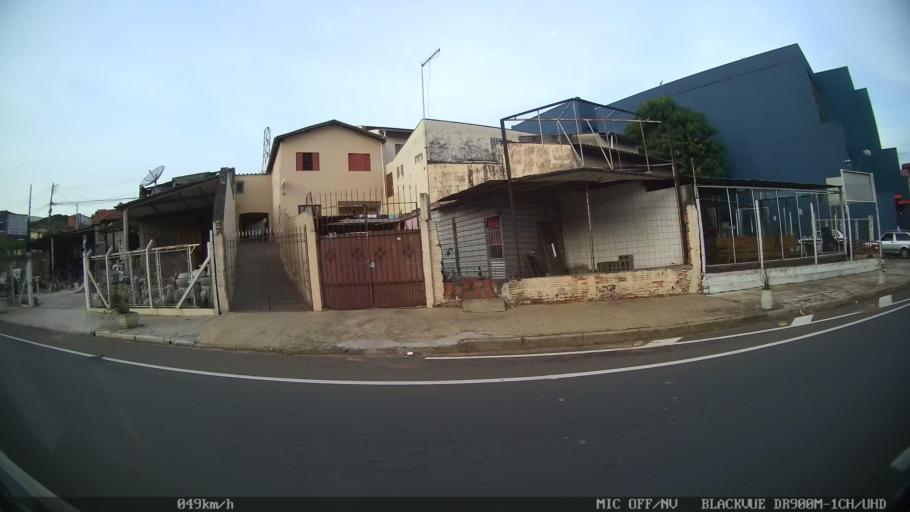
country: BR
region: Sao Paulo
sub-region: Limeira
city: Limeira
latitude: -22.5733
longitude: -47.4146
